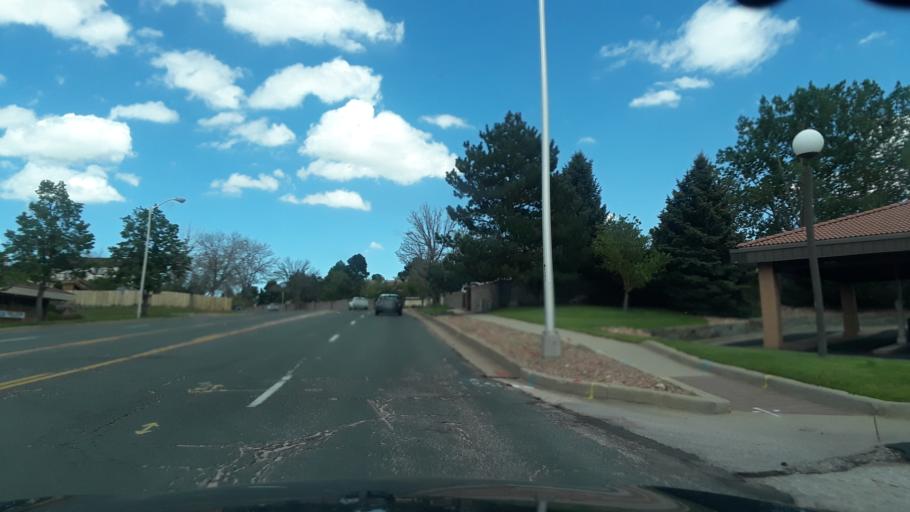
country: US
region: Colorado
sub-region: El Paso County
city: Black Forest
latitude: 38.9417
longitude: -104.7737
